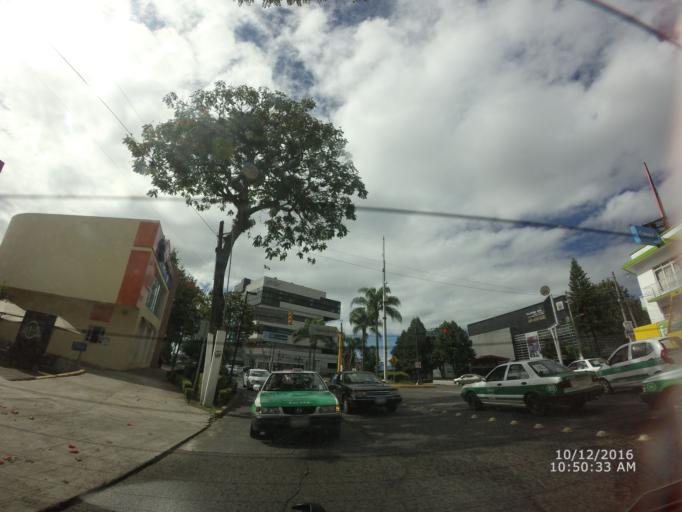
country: TR
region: Sivas
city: Karayun
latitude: 39.6718
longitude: 37.2444
